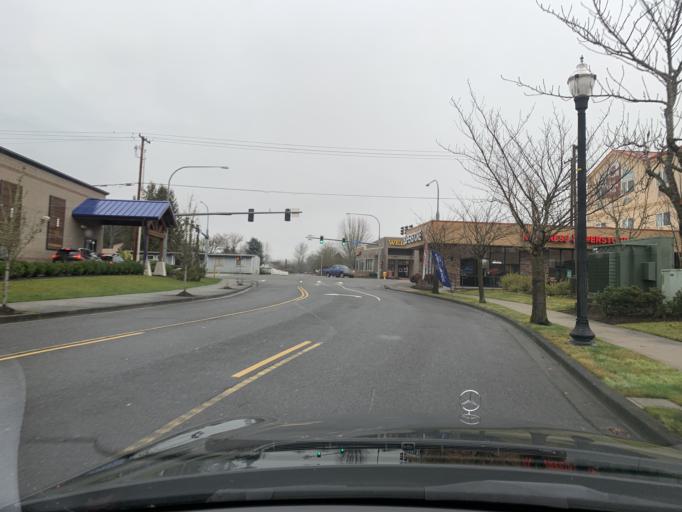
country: US
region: Washington
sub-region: Clark County
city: Battle Ground
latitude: 45.7800
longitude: -122.5530
